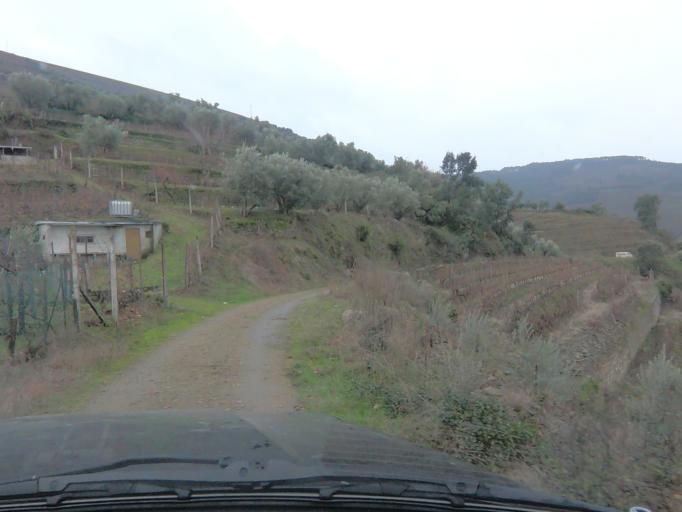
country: PT
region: Vila Real
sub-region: Vila Real
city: Vila Real
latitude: 41.2350
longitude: -7.7386
